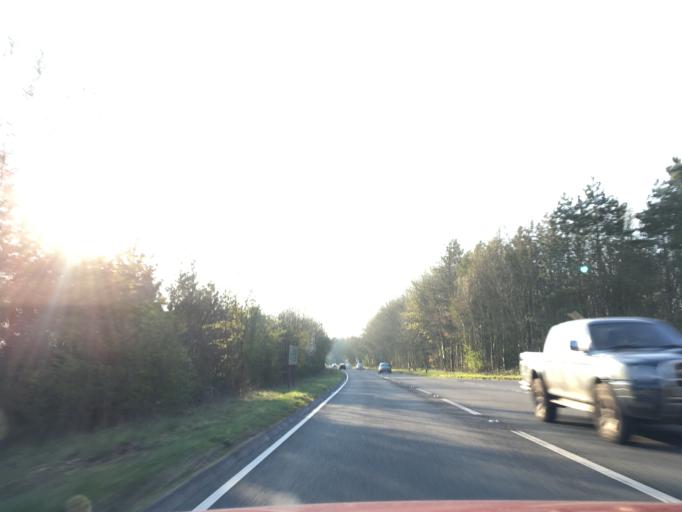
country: GB
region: England
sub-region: Gloucestershire
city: Northleach
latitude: 51.8278
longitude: -1.8099
